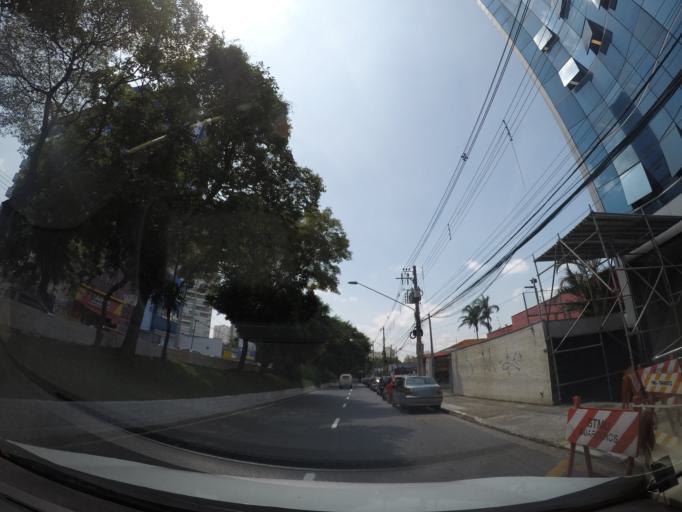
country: BR
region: Sao Paulo
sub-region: Guarulhos
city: Guarulhos
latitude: -23.4611
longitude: -46.5321
